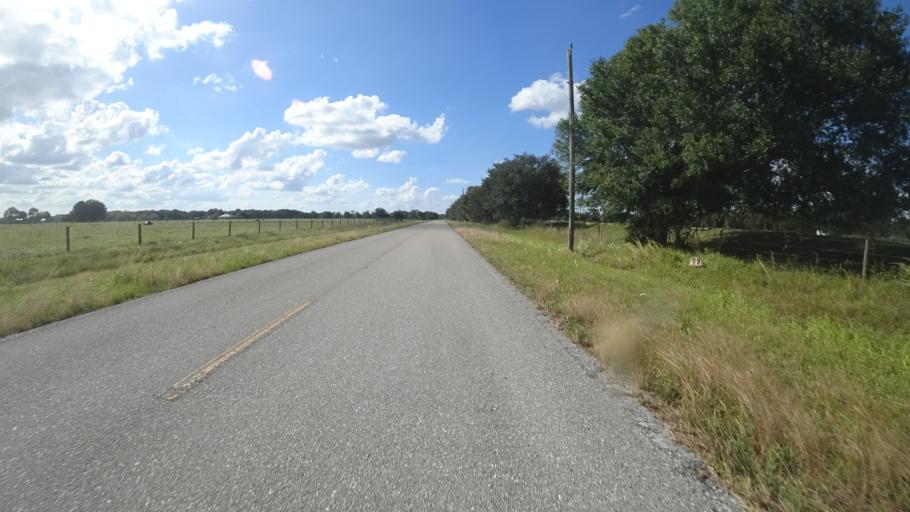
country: US
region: Florida
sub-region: DeSoto County
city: Nocatee
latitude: 27.2709
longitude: -82.0992
